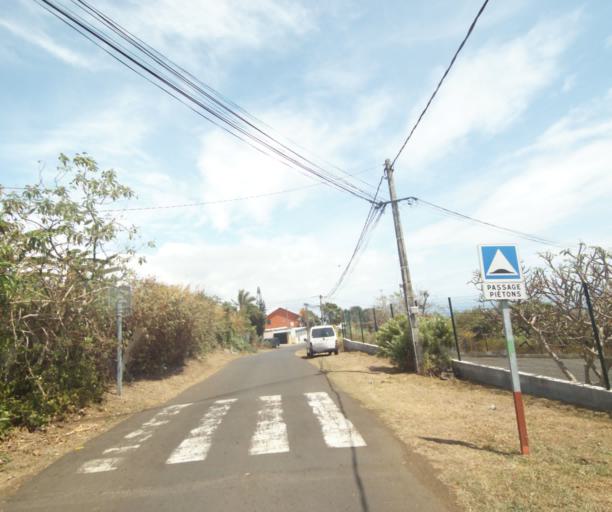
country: RE
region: Reunion
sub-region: Reunion
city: Trois-Bassins
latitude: -21.0980
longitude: 55.2774
